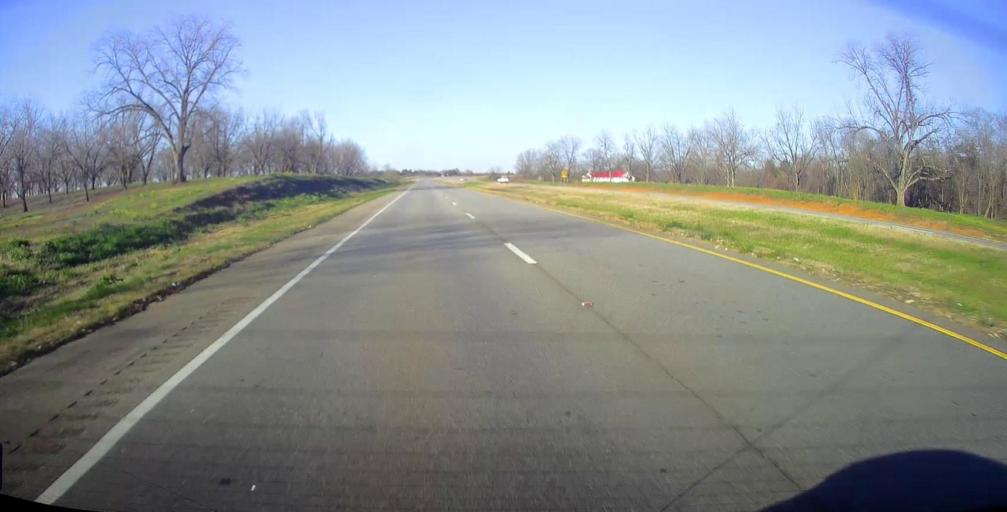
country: US
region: Georgia
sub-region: Sumter County
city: Americus
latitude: 31.9610
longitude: -84.2551
